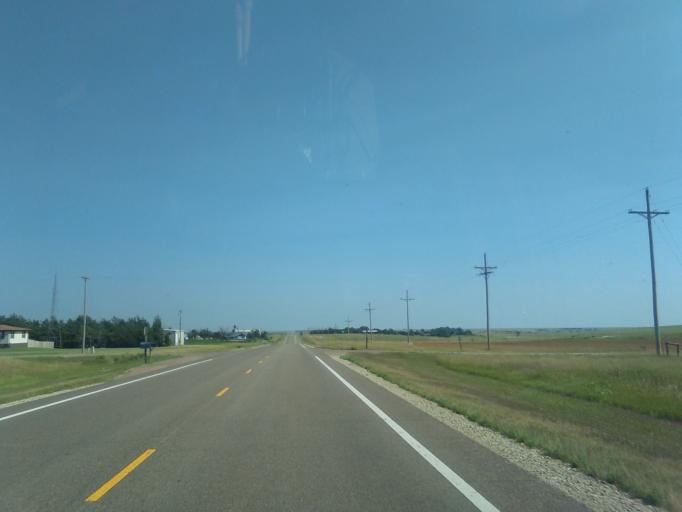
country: US
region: Kansas
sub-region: Sherman County
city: Goodland
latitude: 39.4087
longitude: -101.7075
